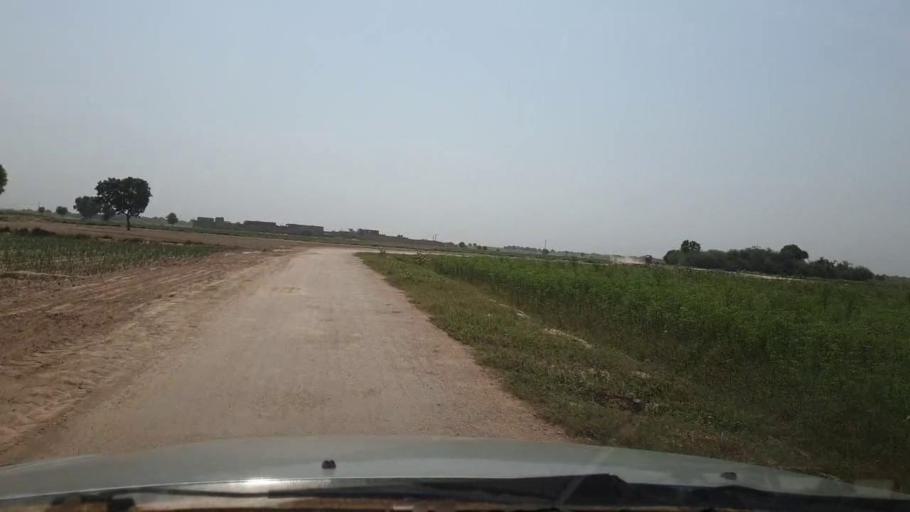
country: PK
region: Sindh
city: Chambar
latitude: 25.2631
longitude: 68.7576
